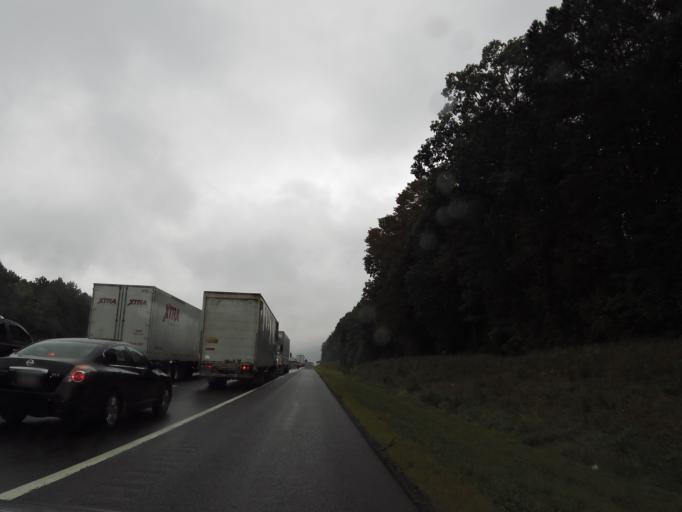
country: US
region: Tennessee
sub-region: Bradley County
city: Hopewell
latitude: 35.2214
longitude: -84.8607
